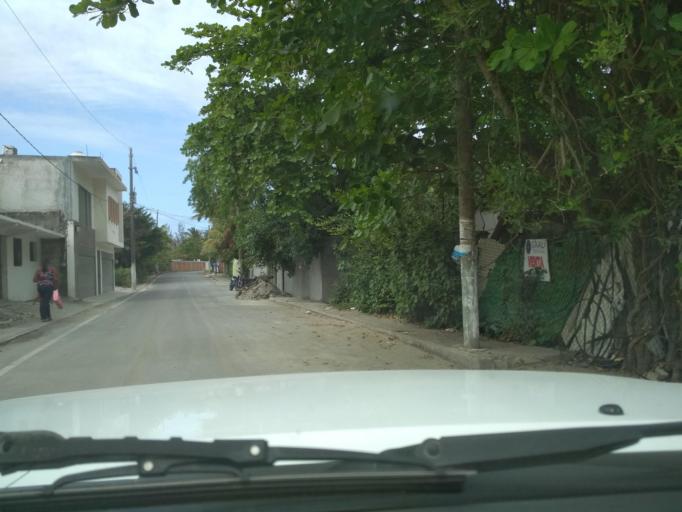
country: MX
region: Veracruz
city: Anton Lizardo
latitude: 19.0322
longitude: -95.9689
